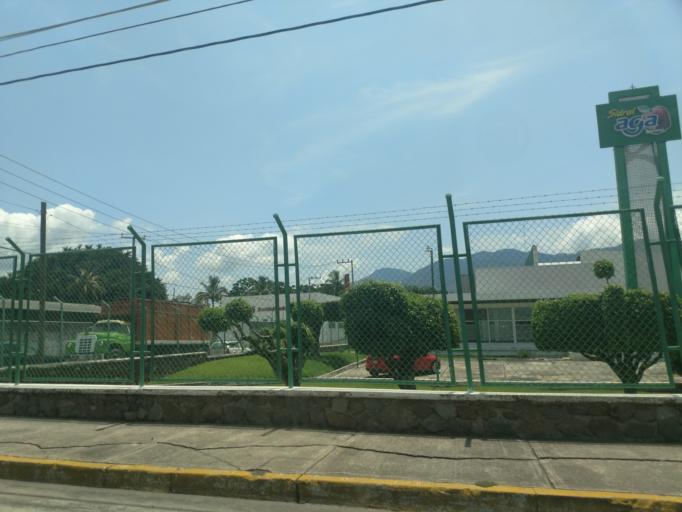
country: MX
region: Nayarit
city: Tepic
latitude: 21.4926
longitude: -104.8790
